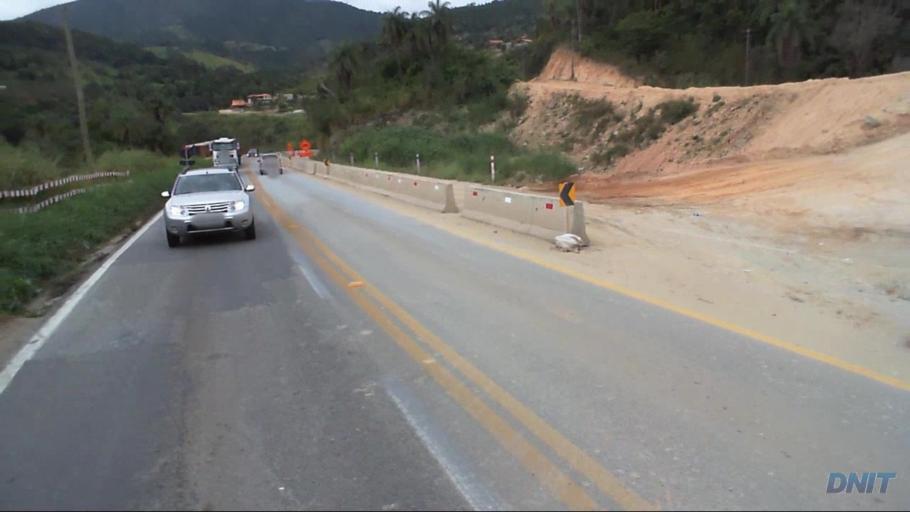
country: BR
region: Minas Gerais
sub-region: Caete
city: Caete
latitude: -19.7835
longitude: -43.6662
